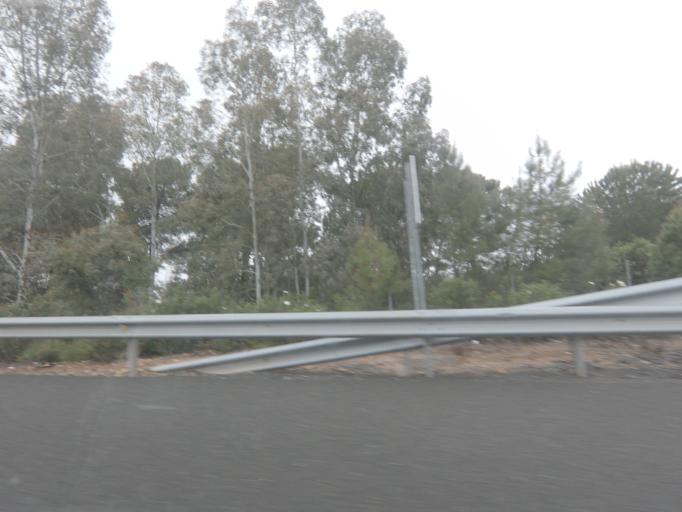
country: ES
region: Extremadura
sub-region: Provincia de Caceres
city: Casas de Millan
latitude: 39.8283
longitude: -6.3618
